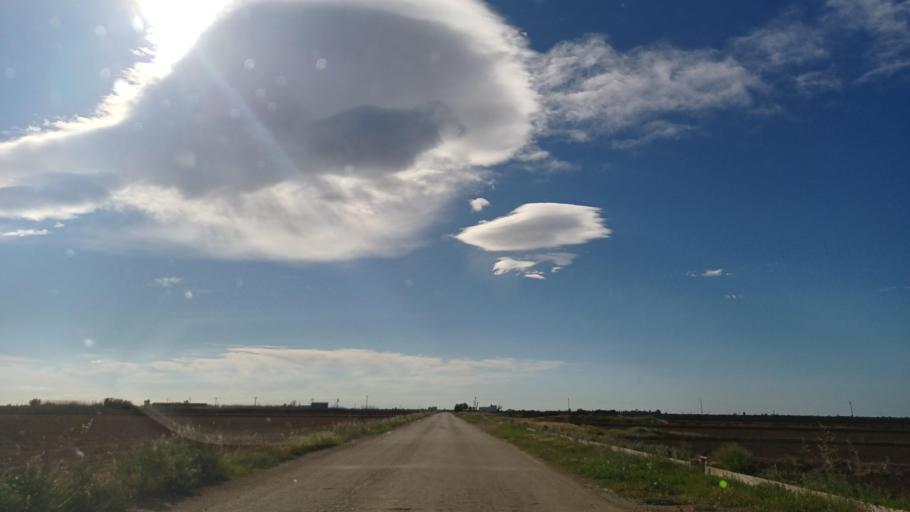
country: ES
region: Catalonia
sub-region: Provincia de Tarragona
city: L'Ampolla
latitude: 40.7723
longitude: 0.6967
